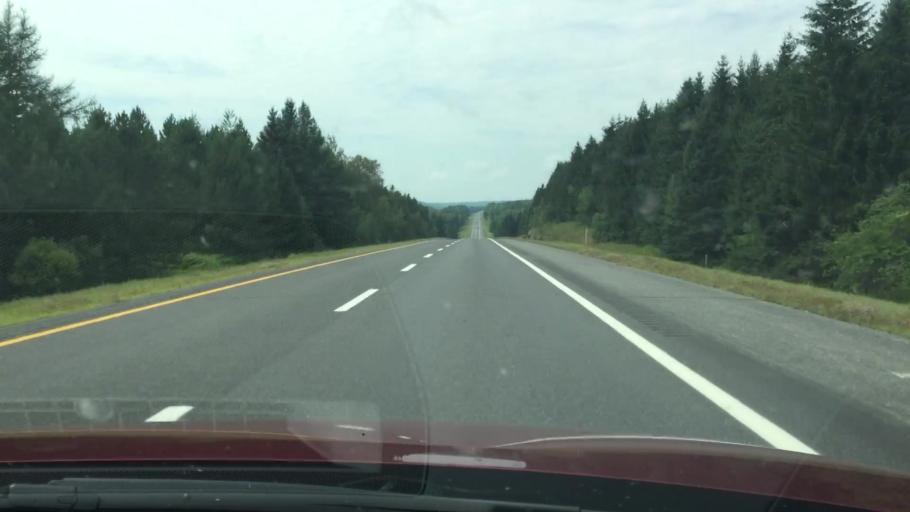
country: US
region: Maine
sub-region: Aroostook County
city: Houlton
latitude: 46.1412
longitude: -67.9746
